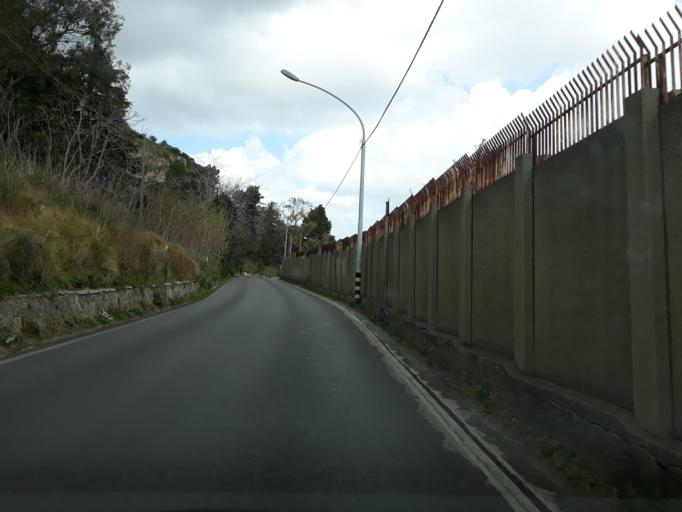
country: IT
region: Sicily
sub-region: Palermo
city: Monreale
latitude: 38.1037
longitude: 13.3102
